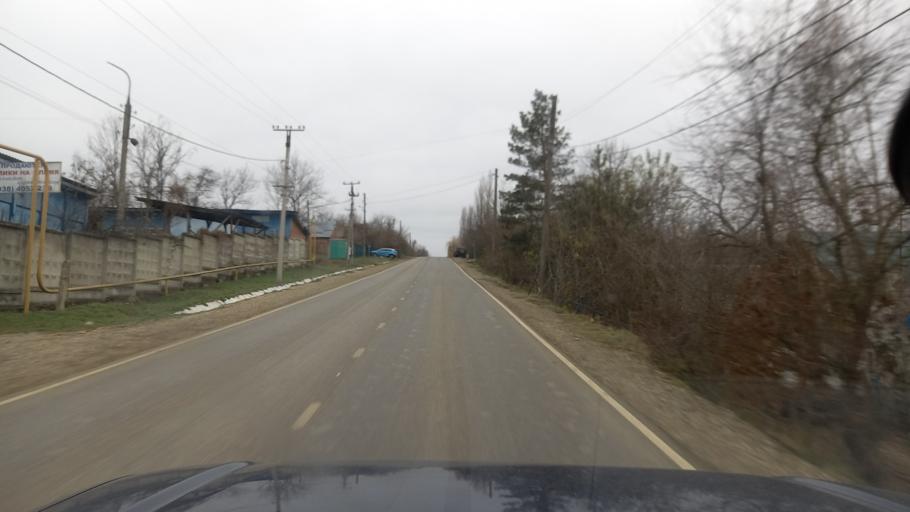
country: RU
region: Krasnodarskiy
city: Saratovskaya
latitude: 44.5321
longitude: 39.2941
